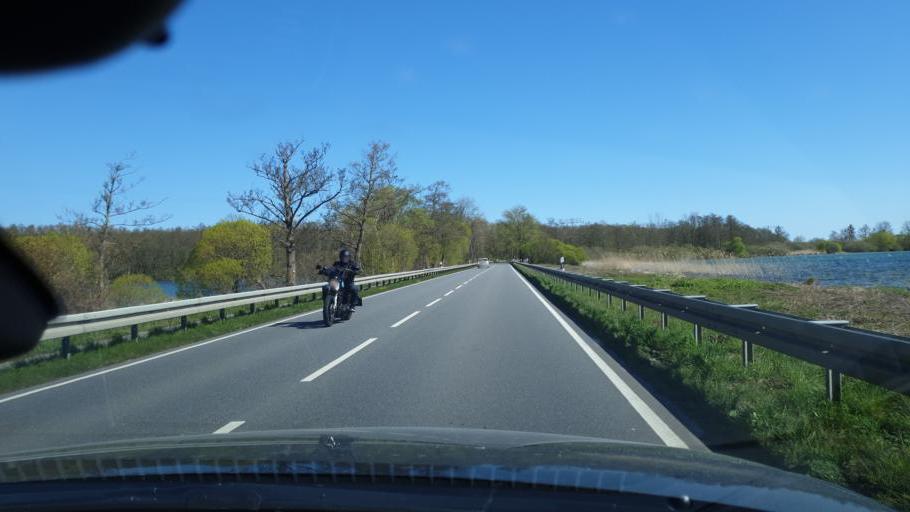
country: DE
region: Mecklenburg-Vorpommern
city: Seehof
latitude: 53.6820
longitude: 11.4634
